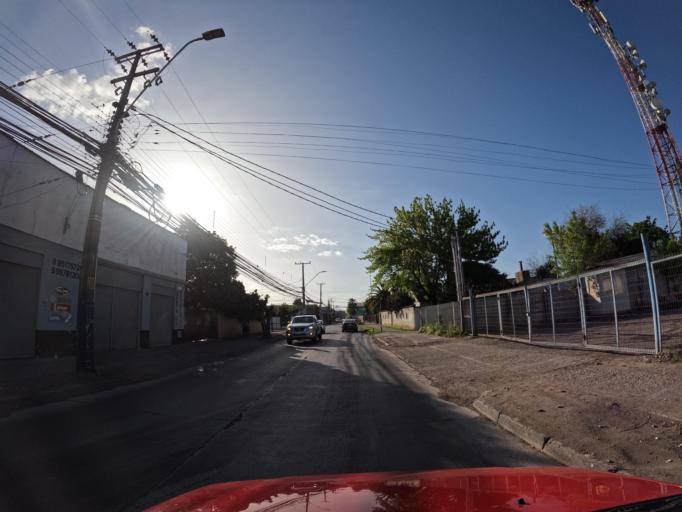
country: CL
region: O'Higgins
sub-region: Provincia de Colchagua
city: Santa Cruz
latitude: -34.6439
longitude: -71.3653
